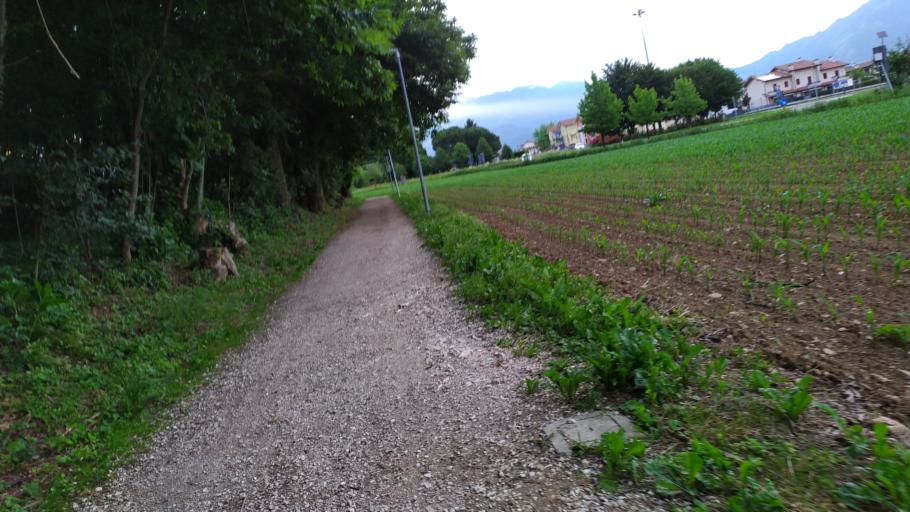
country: IT
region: Veneto
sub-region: Provincia di Vicenza
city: Malo
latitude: 45.6650
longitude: 11.3967
